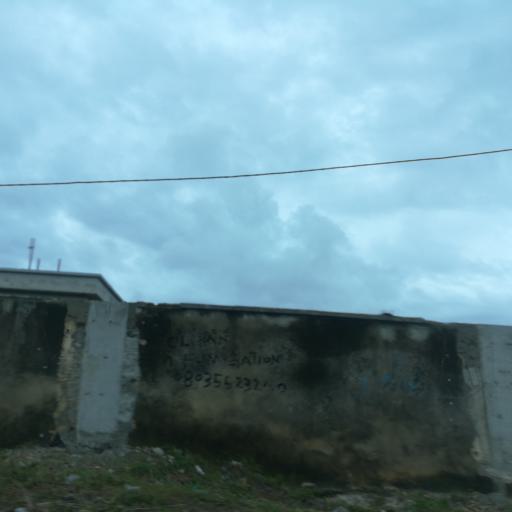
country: NG
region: Lagos
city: Ikoyi
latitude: 6.4477
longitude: 3.4678
